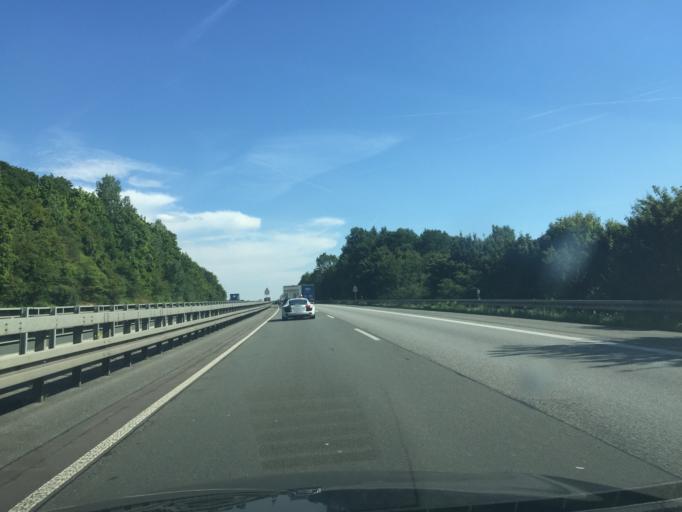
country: DE
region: Hesse
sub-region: Regierungsbezirk Giessen
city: Sinn
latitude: 50.6314
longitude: 8.3315
